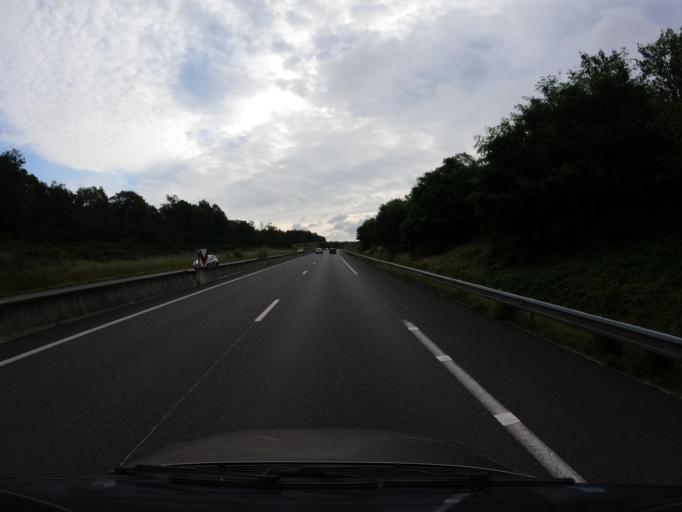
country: FR
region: Centre
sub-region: Departement d'Indre-et-Loire
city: Langeais
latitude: 47.3457
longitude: 0.4018
